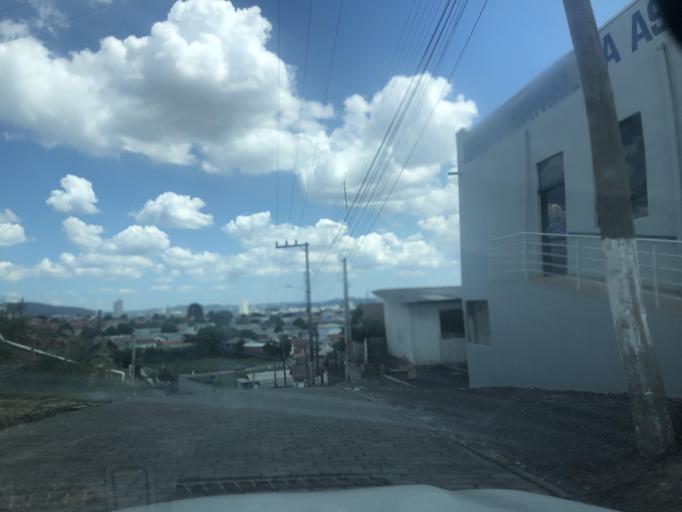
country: BR
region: Santa Catarina
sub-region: Lages
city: Lages
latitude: -27.7882
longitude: -50.3120
